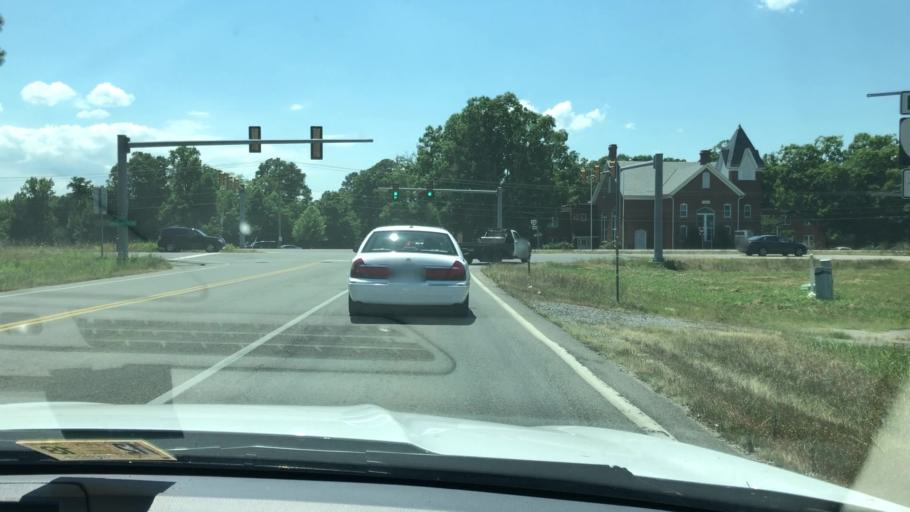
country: US
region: Virginia
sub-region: Middlesex County
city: Saluda
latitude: 37.5821
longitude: -76.4866
